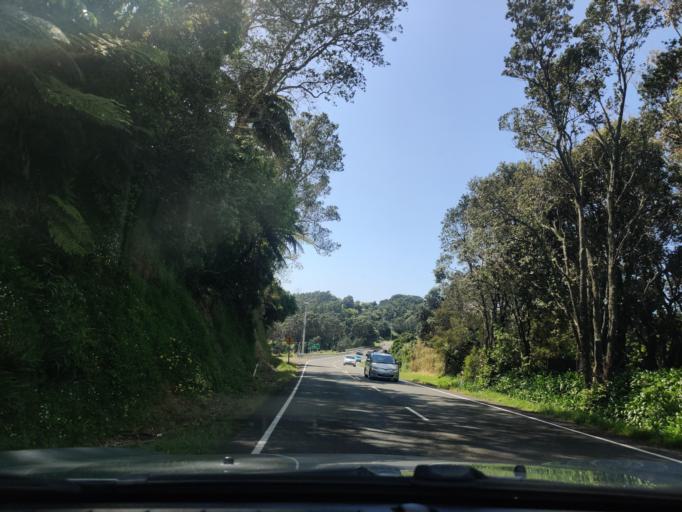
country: NZ
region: Taranaki
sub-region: New Plymouth District
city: New Plymouth
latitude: -39.1138
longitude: 173.9582
